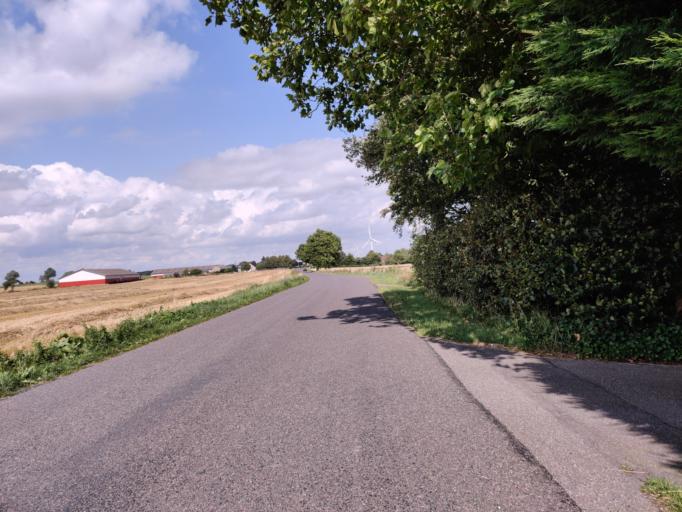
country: DK
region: Zealand
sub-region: Guldborgsund Kommune
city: Nykobing Falster
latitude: 54.6639
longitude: 11.8906
